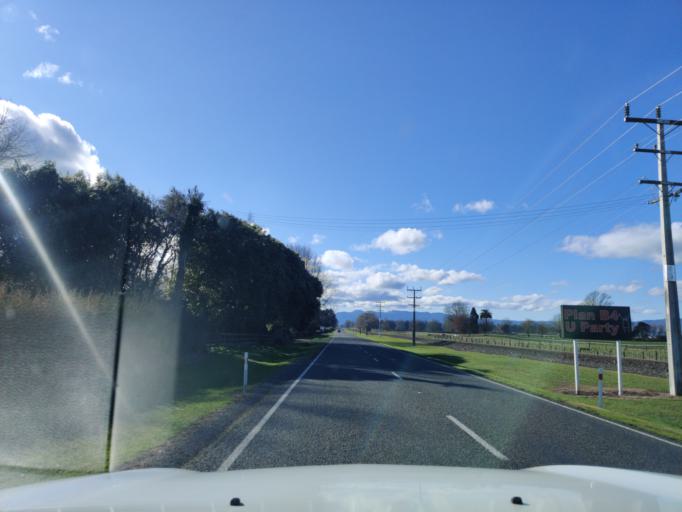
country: NZ
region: Waikato
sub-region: Matamata-Piako District
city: Matamata
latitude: -37.8586
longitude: 175.7557
